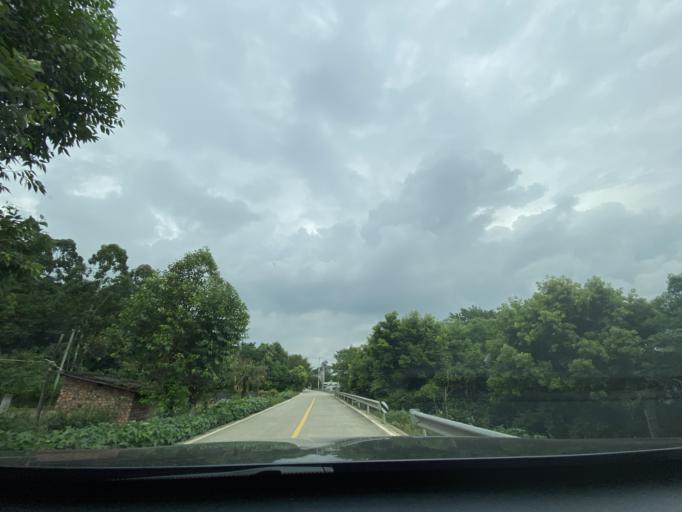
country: CN
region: Sichuan
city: Wujin
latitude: 30.3931
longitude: 103.9668
